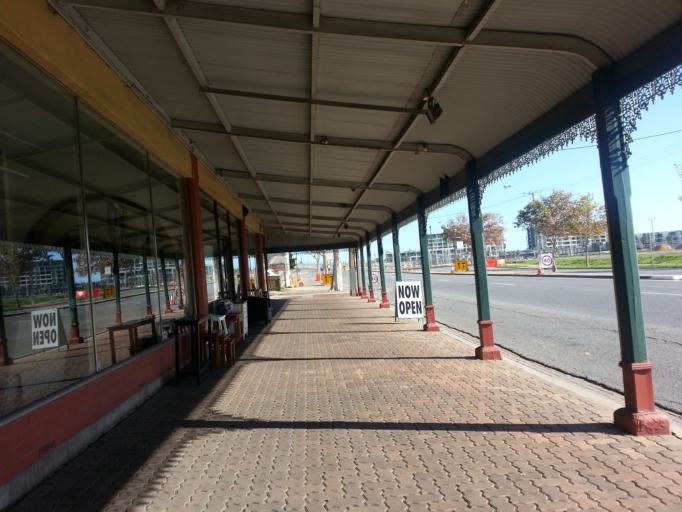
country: AU
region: South Australia
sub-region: Port Adelaide Enfield
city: Birkenhead
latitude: -34.8456
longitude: 138.4997
